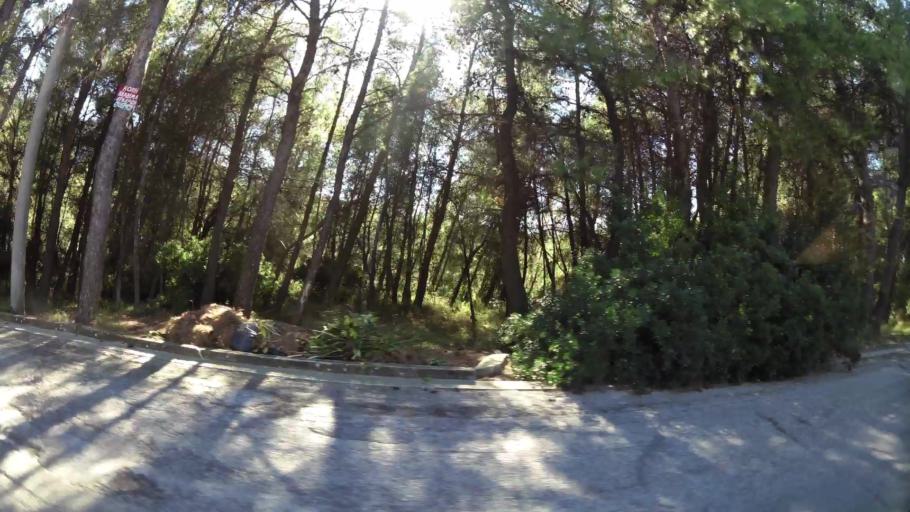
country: GR
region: Attica
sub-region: Nomarchia Athinas
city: Ekali
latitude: 38.1158
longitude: 23.8476
